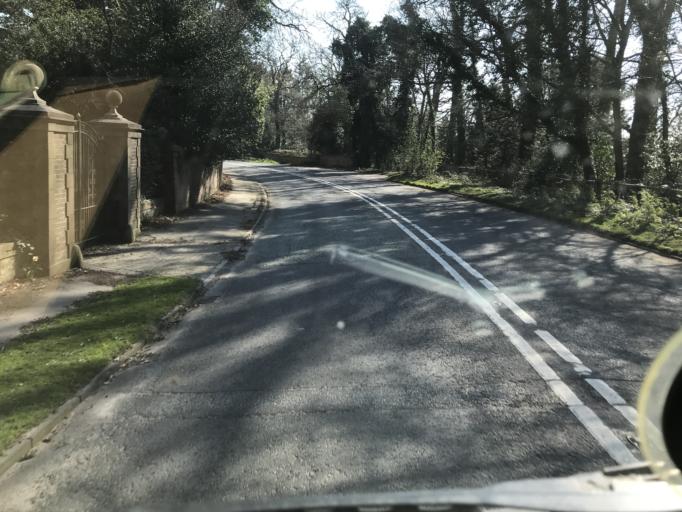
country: GB
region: England
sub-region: Cheshire East
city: Knutsford
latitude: 53.2887
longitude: -2.3470
